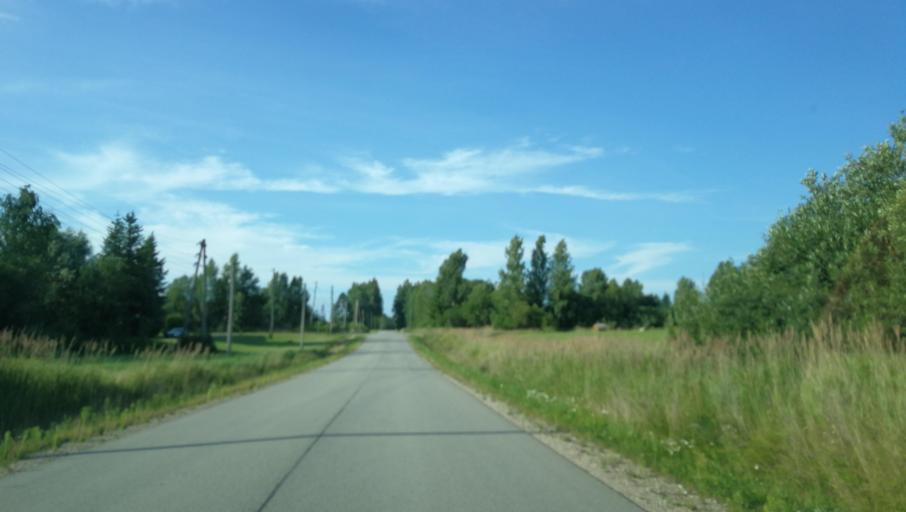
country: LV
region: Pargaujas
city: Stalbe
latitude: 57.3356
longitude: 25.1338
